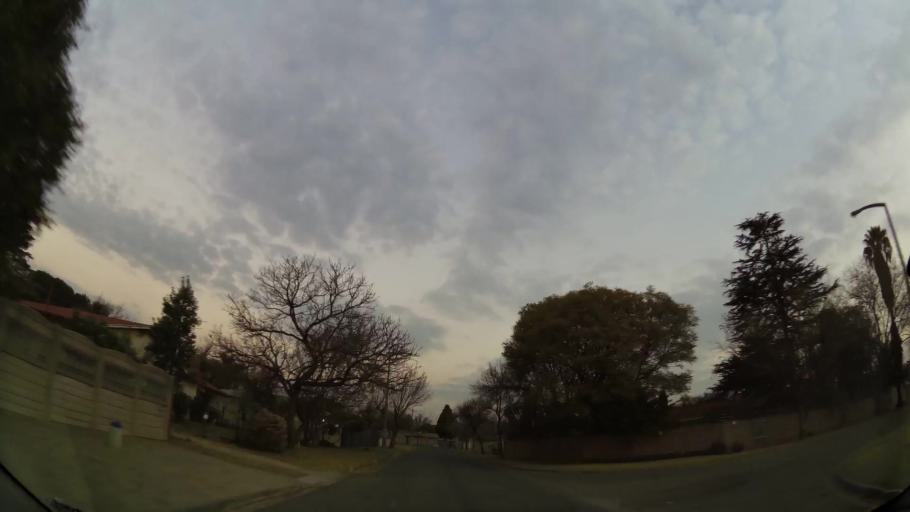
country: ZA
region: Gauteng
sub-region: Ekurhuleni Metropolitan Municipality
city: Benoni
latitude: -26.1467
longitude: 28.3018
